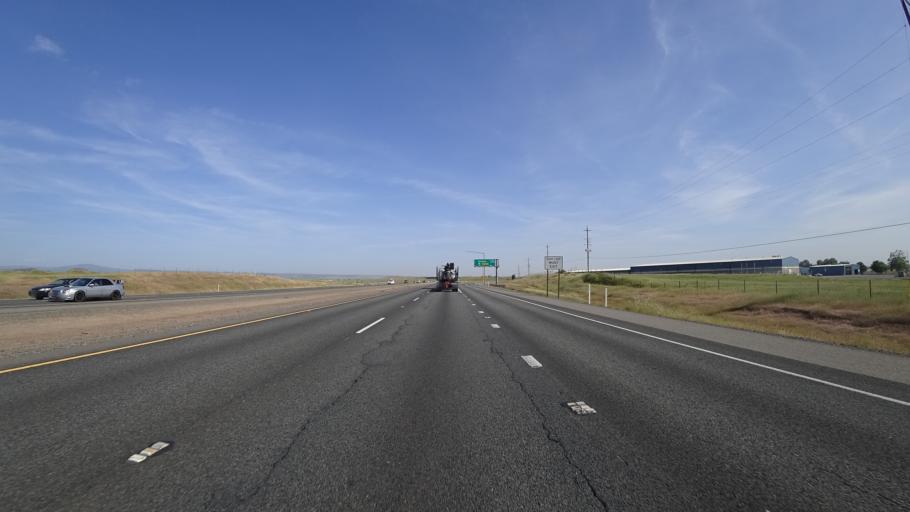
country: US
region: California
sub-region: Butte County
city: Durham
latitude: 39.6466
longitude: -121.7213
